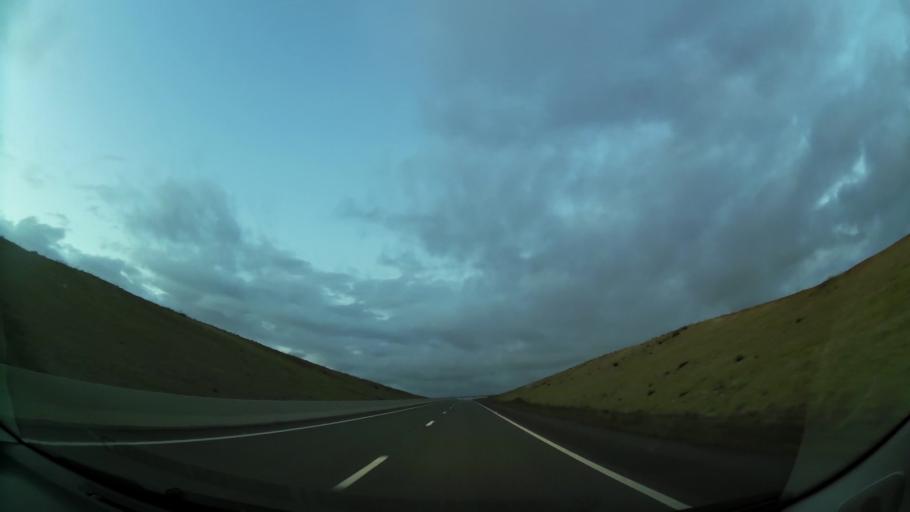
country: MA
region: Oriental
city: El Aioun
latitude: 34.6191
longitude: -2.4043
